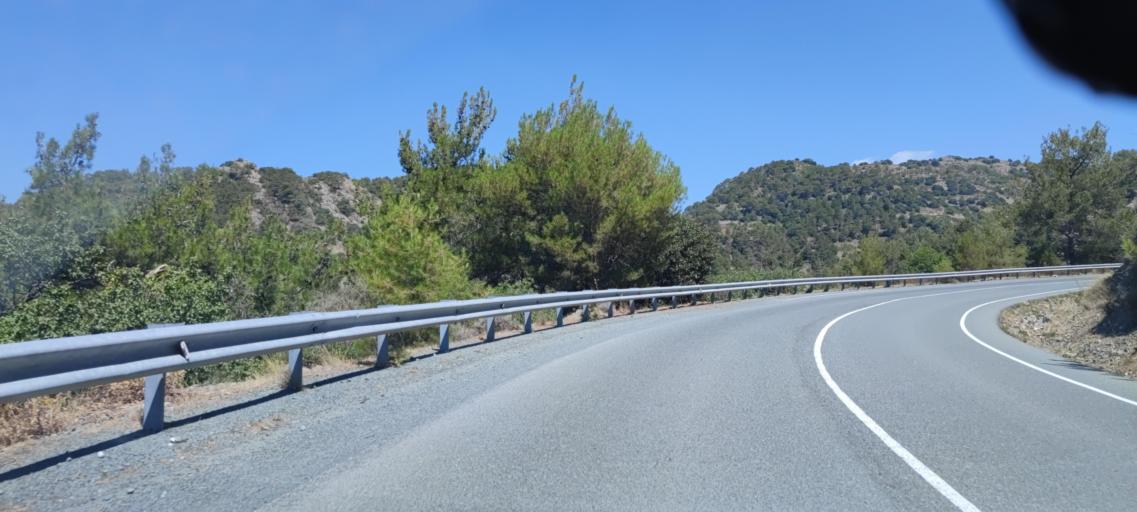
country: CY
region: Lefkosia
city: Kakopetria
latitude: 34.9027
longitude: 32.8142
